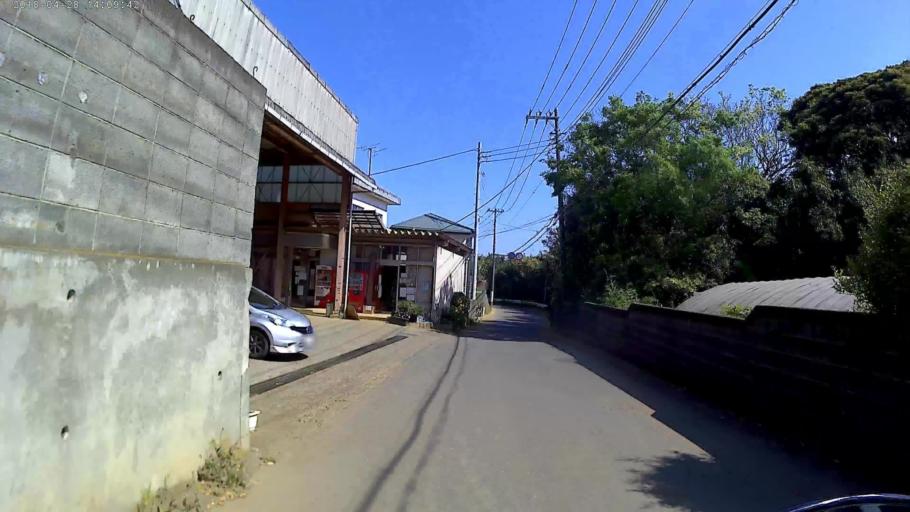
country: JP
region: Kanagawa
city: Miura
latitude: 35.1456
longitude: 139.6522
